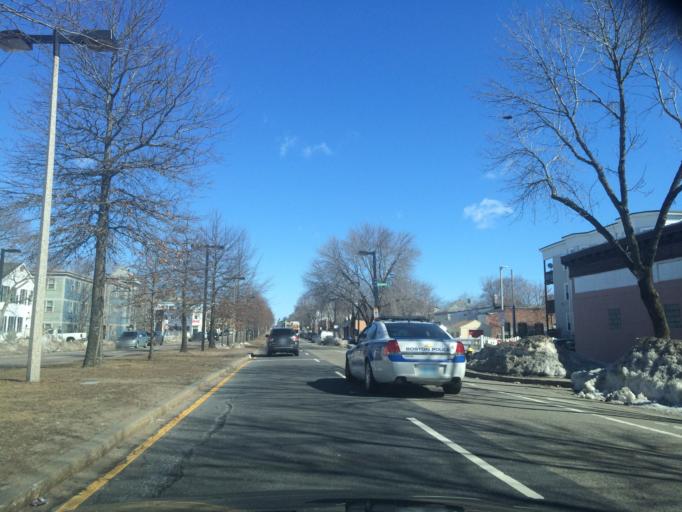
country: US
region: Massachusetts
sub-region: Suffolk County
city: Jamaica Plain
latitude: 42.2875
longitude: -71.0904
